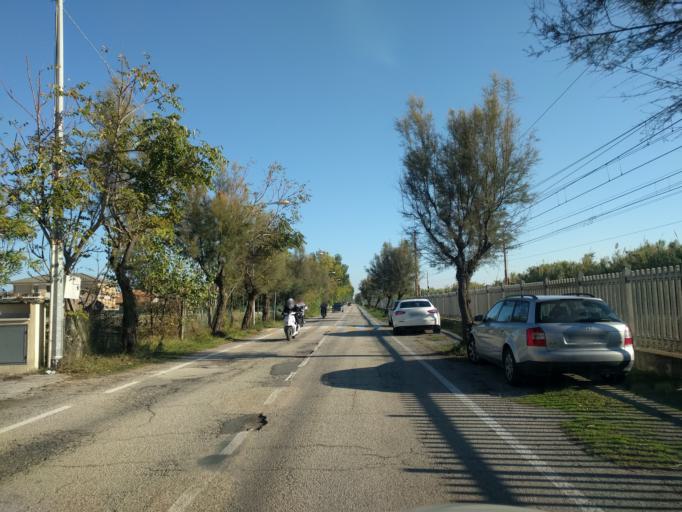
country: IT
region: The Marches
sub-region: Provincia di Pesaro e Urbino
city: Marotta
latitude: 43.7962
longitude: 13.0984
